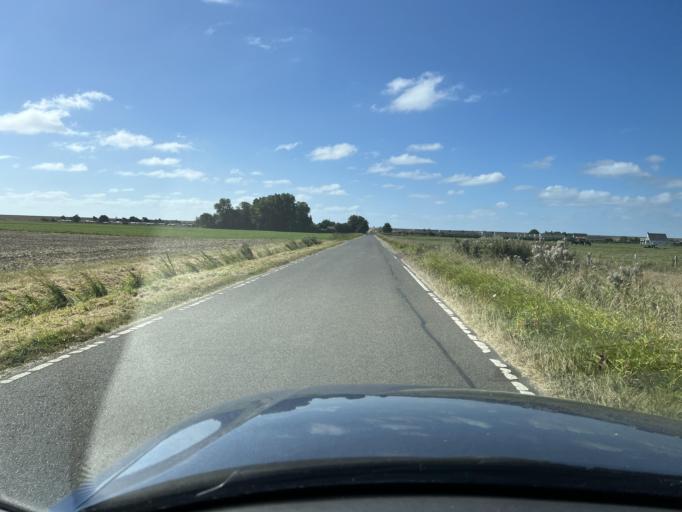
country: DE
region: Schleswig-Holstein
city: Wesselburenerkoog
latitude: 54.2466
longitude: 8.8489
